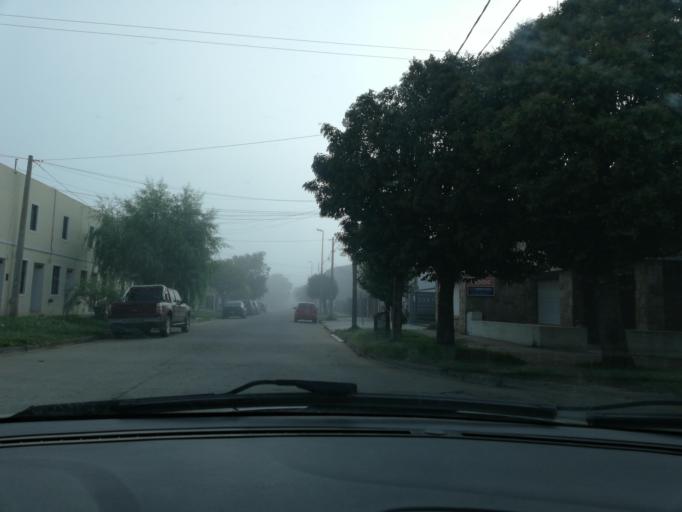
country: AR
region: Buenos Aires
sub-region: Partido de Balcarce
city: Balcarce
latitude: -37.8542
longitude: -58.2630
